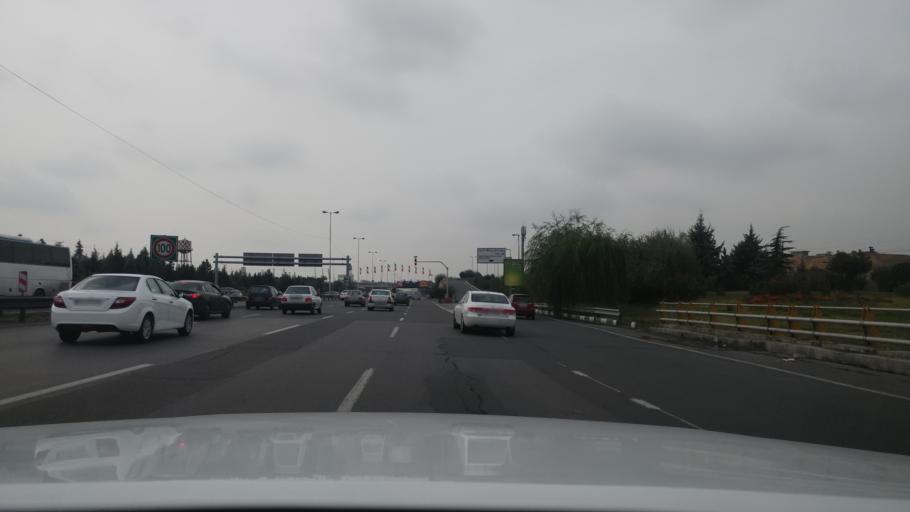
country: IR
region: Tehran
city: Tehran
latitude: 35.7164
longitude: 51.2910
